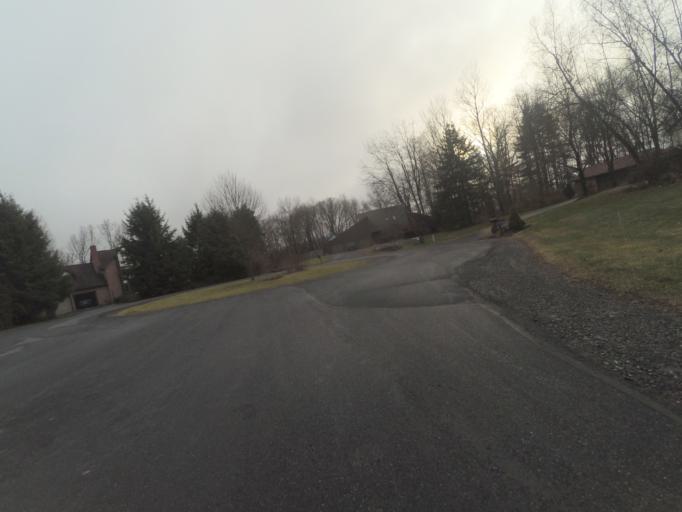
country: US
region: Pennsylvania
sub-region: Centre County
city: Park Forest Village
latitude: 40.7784
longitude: -77.9206
